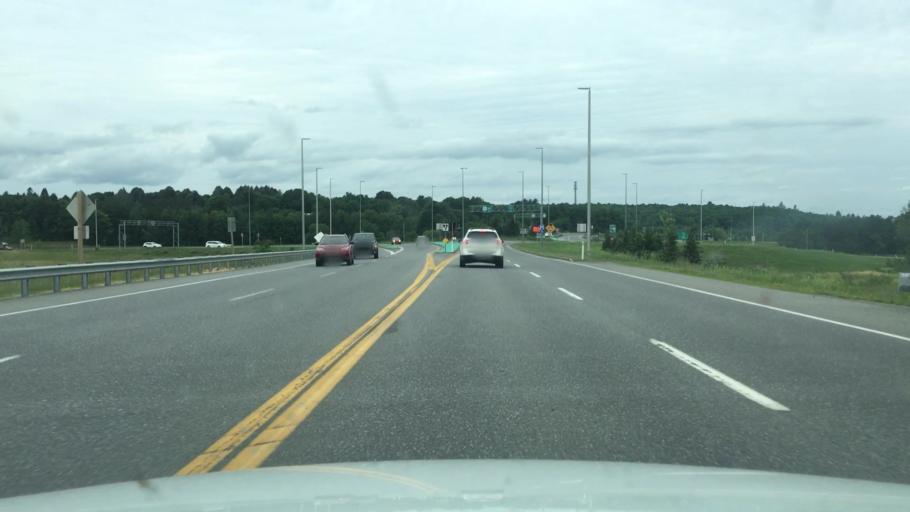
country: US
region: Maine
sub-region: Kennebec County
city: Augusta
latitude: 44.3523
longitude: -69.7790
